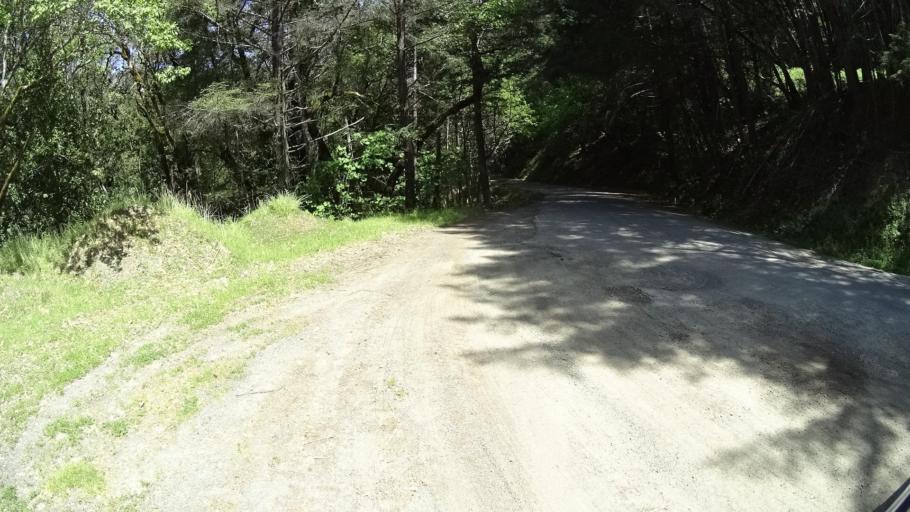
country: US
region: California
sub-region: Humboldt County
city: Redway
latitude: 40.1989
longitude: -123.5198
